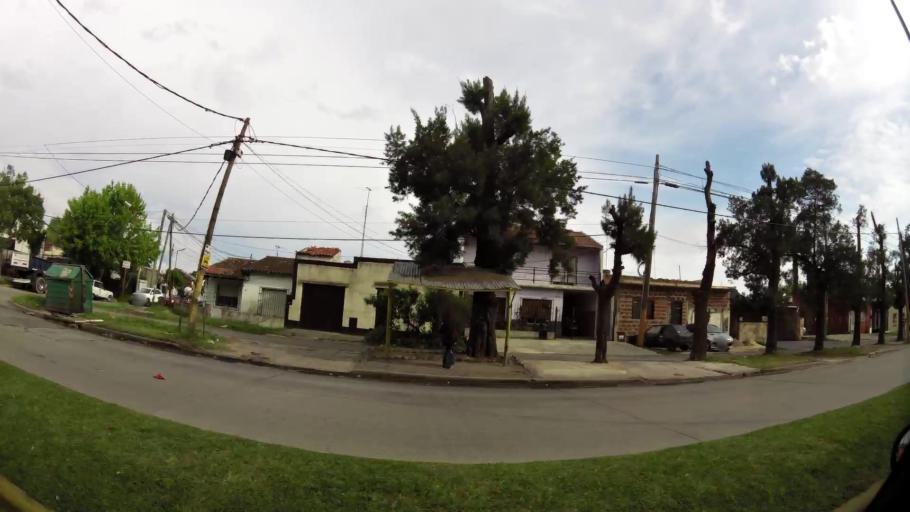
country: AR
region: Buenos Aires
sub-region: Partido de Quilmes
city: Quilmes
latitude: -34.7139
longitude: -58.2426
